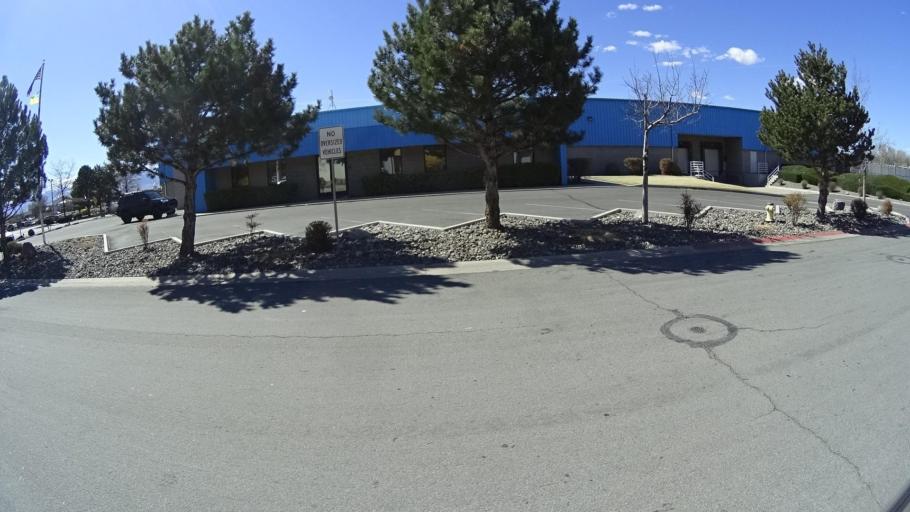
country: US
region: Nevada
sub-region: Washoe County
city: Sparks
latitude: 39.5340
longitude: -119.7137
